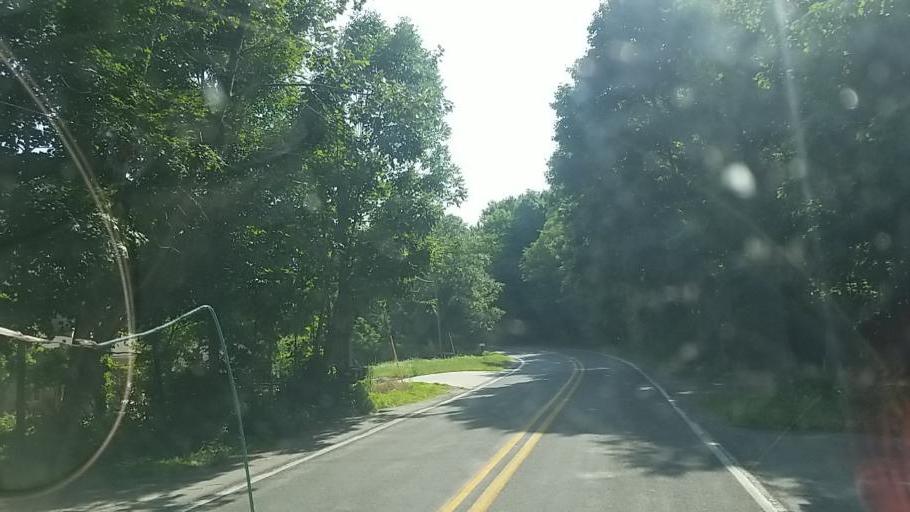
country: US
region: Michigan
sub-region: Muskegon County
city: Montague
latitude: 43.3660
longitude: -86.3945
